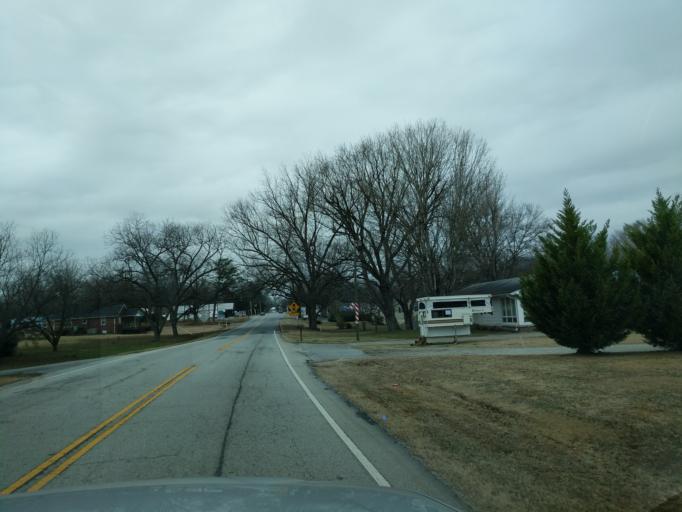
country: US
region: South Carolina
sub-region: Spartanburg County
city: Duncan
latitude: 34.8633
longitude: -82.1109
